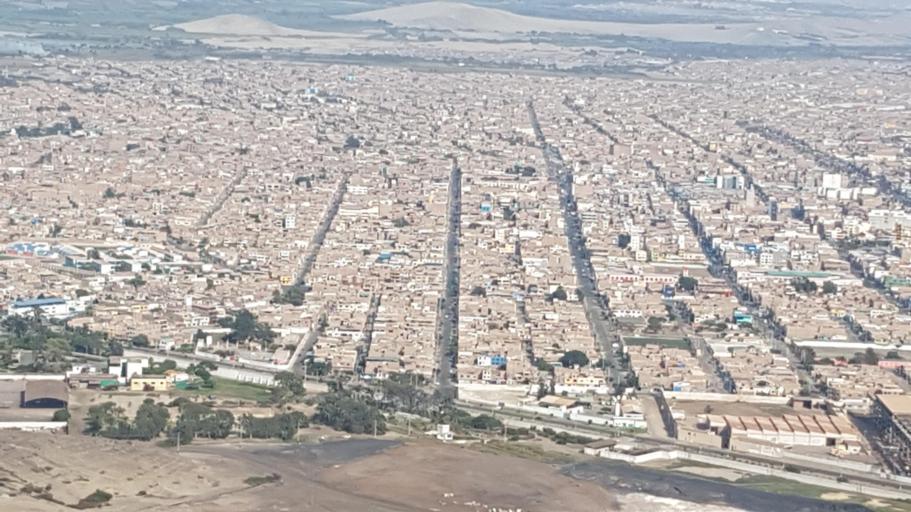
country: PE
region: Ancash
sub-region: Provincia de Santa
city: Chimbote
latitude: -9.0644
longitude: -78.6139
